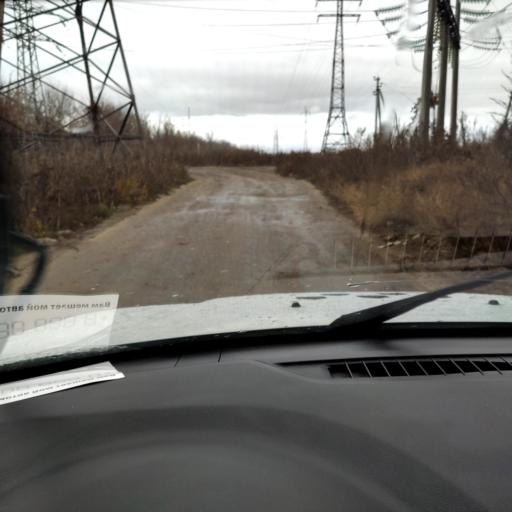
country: RU
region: Samara
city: Tol'yatti
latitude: 53.5516
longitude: 49.4467
